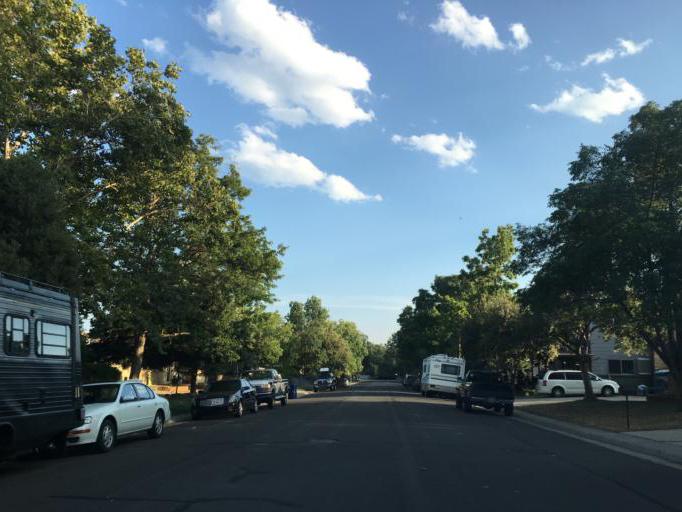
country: US
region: Colorado
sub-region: Jefferson County
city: Applewood
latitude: 39.7933
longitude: -105.1474
